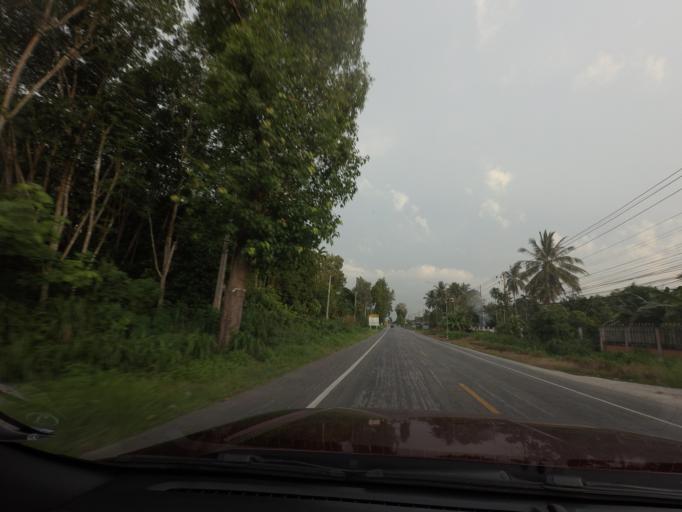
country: TH
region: Pattani
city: Mae Lan
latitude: 6.5869
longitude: 101.1967
